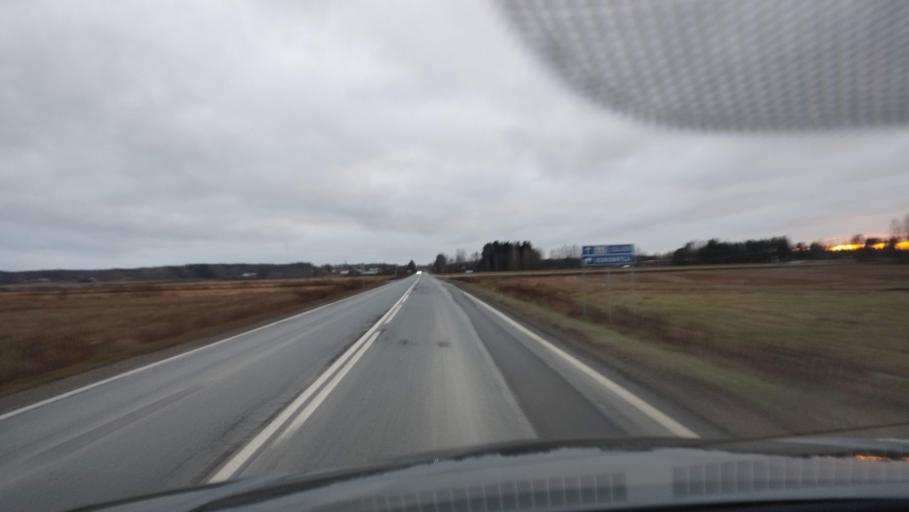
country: FI
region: Southern Ostrobothnia
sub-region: Suupohja
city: Kauhajoki
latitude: 62.3711
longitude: 22.0782
